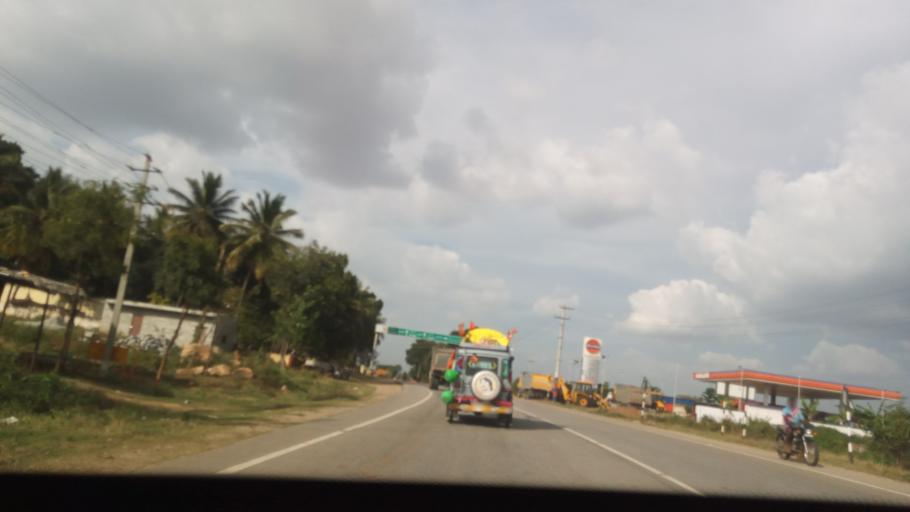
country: IN
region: Karnataka
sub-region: Tumkur
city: Kunigal
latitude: 12.8402
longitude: 77.0350
